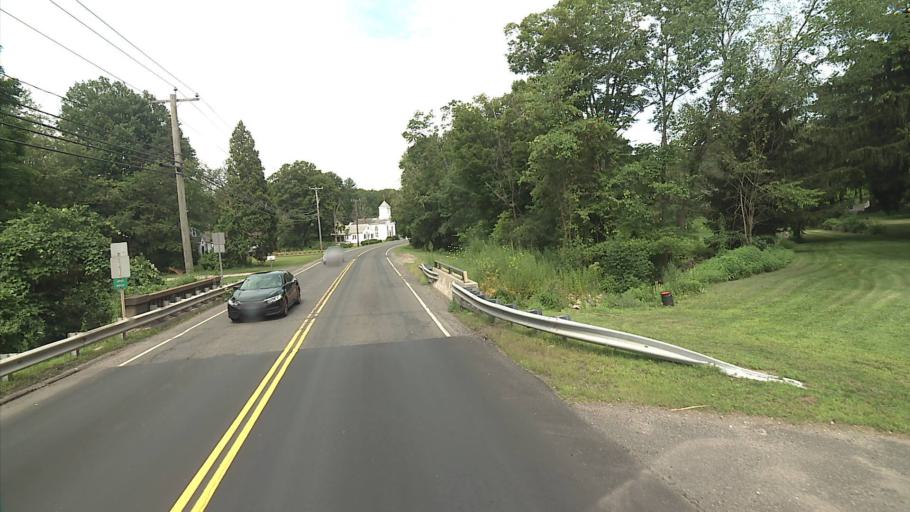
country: US
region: Connecticut
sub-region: New Haven County
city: Oxford
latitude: 41.4330
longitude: -73.1143
